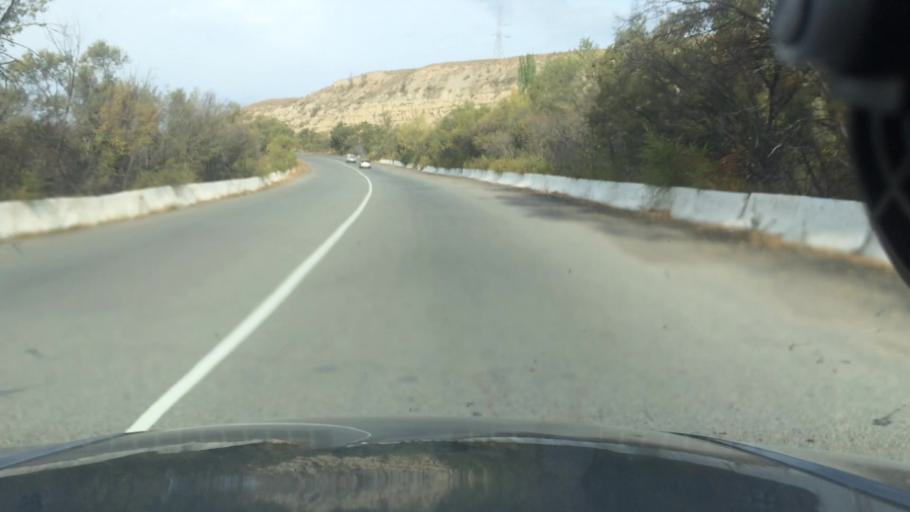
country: KG
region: Ysyk-Koel
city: Karakol
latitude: 42.5941
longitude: 78.3854
